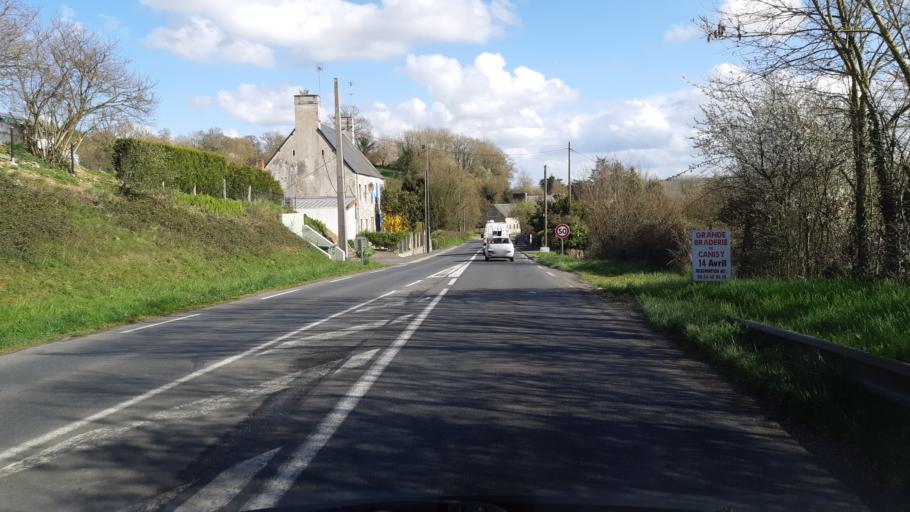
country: FR
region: Lower Normandy
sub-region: Departement de la Manche
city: Agneaux
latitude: 49.0940
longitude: -1.1193
